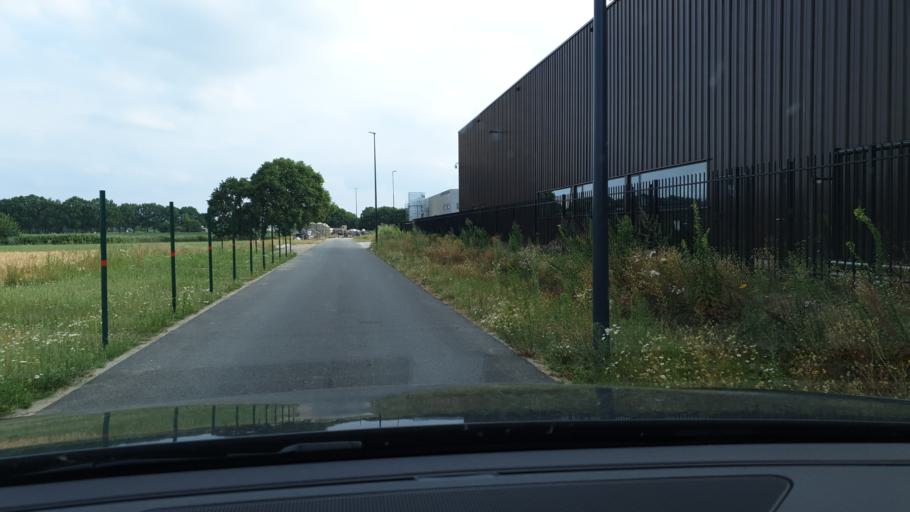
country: NL
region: North Brabant
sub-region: Gemeente Veldhoven
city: Oerle
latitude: 51.4338
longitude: 5.3720
